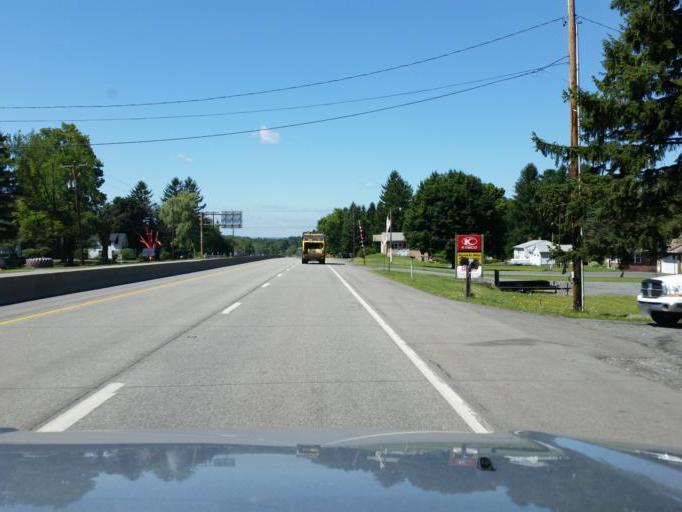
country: US
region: Pennsylvania
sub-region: Cambria County
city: Nanty Glo
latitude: 40.4557
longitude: -78.7793
